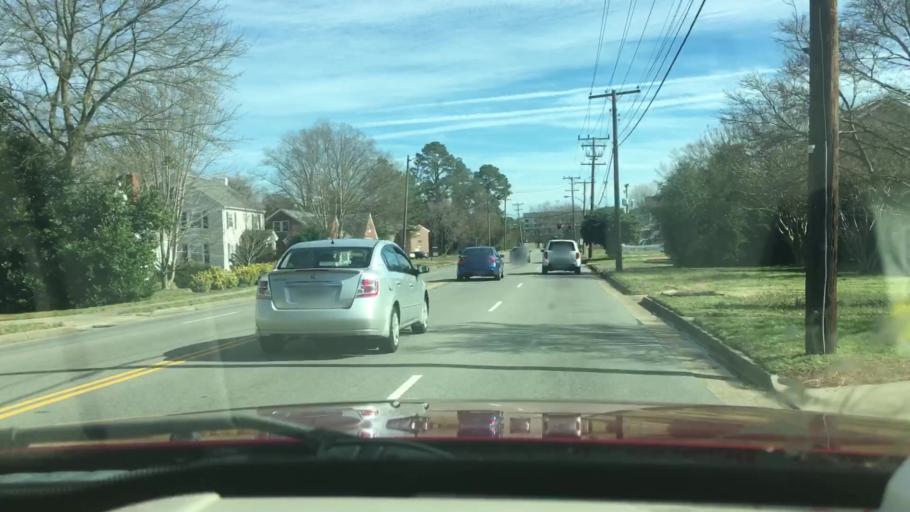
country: US
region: Virginia
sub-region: City of Portsmouth
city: Portsmouth Heights
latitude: 36.8399
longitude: -76.3550
